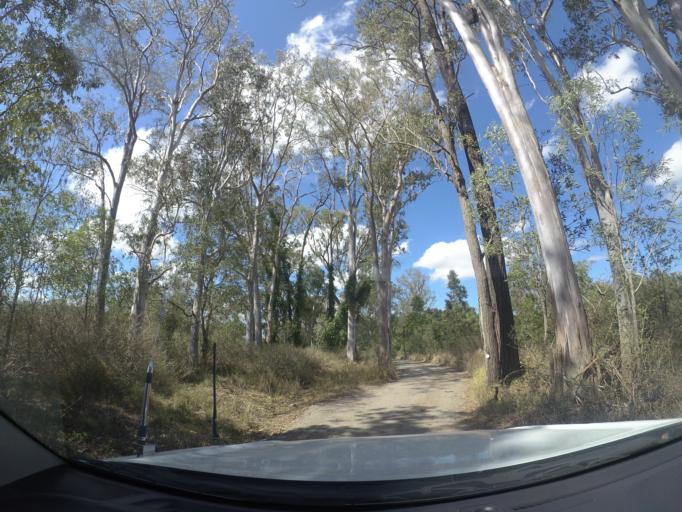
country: AU
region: Queensland
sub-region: Logan
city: Cedar Vale
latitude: -27.8433
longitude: 152.9737
